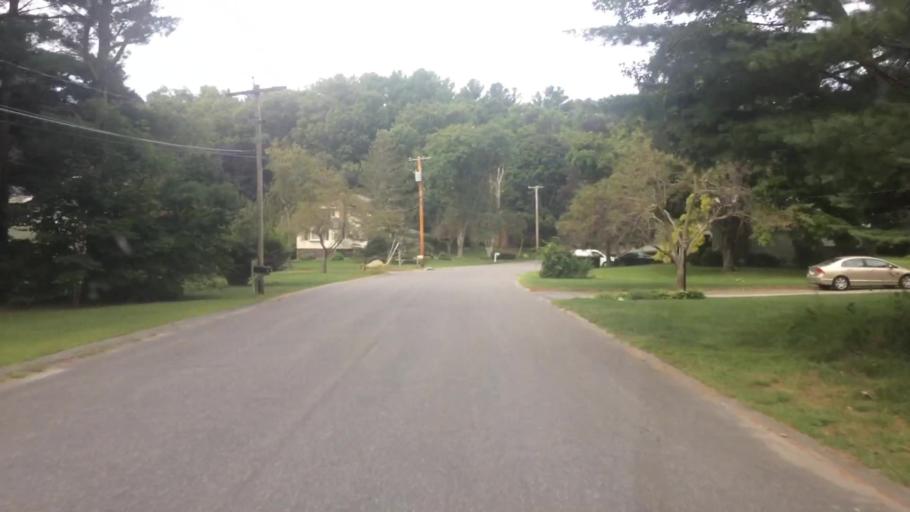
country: US
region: Massachusetts
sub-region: Middlesex County
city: Acton
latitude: 42.4611
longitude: -71.4343
